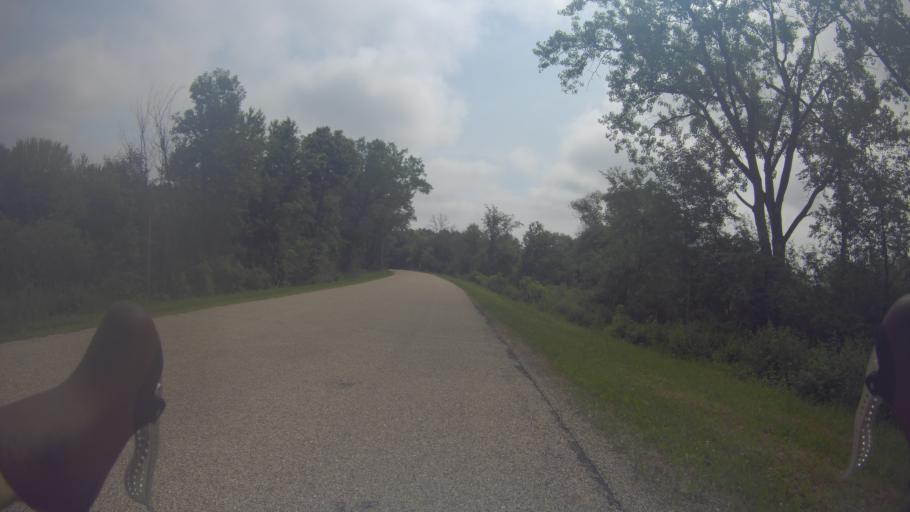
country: US
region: Wisconsin
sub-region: Jefferson County
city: Cambridge
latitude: 42.9205
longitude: -89.0295
